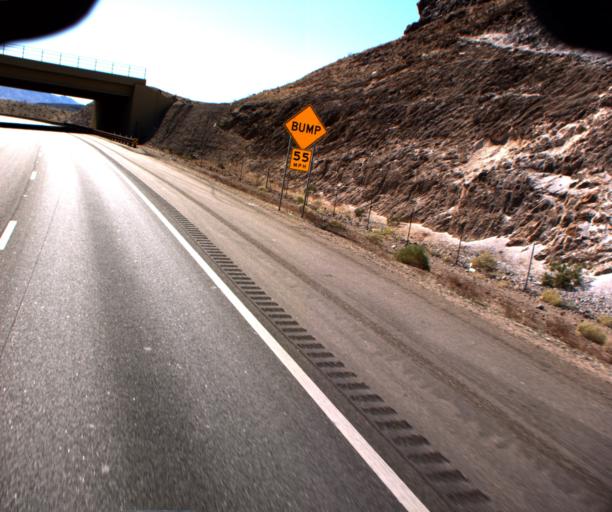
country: US
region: Nevada
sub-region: Clark County
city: Boulder City
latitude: 35.9856
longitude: -114.7128
